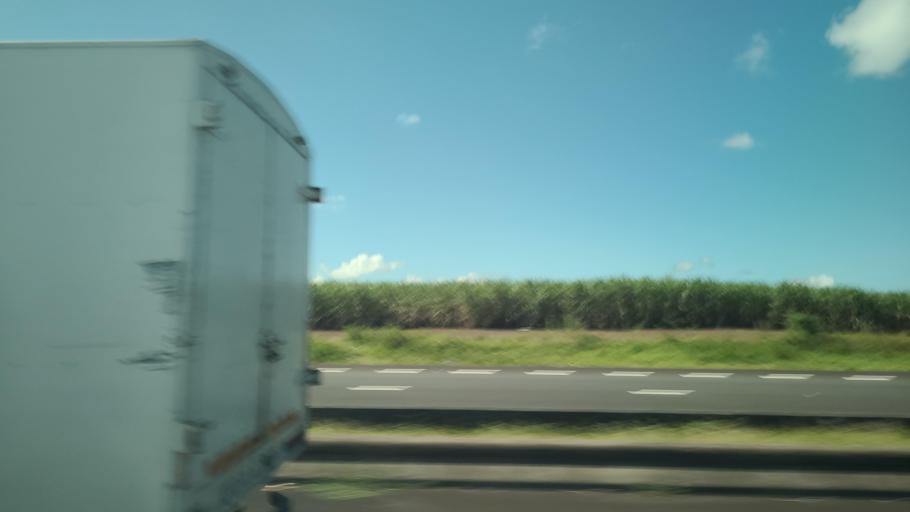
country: MU
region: Grand Port
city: Plaine Magnien
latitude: -20.4389
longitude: 57.6626
